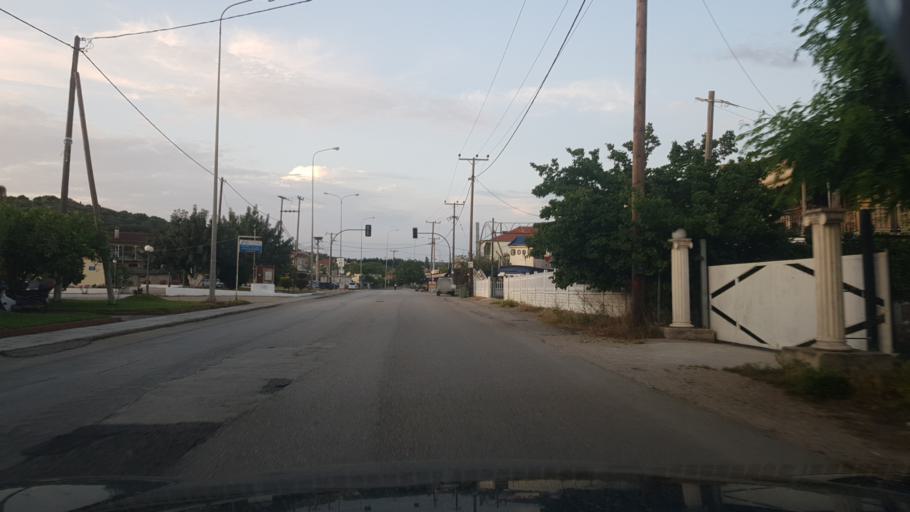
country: GR
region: West Greece
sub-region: Nomos Aitolias kai Akarnanias
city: Vonitsa
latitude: 38.8684
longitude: 20.8039
